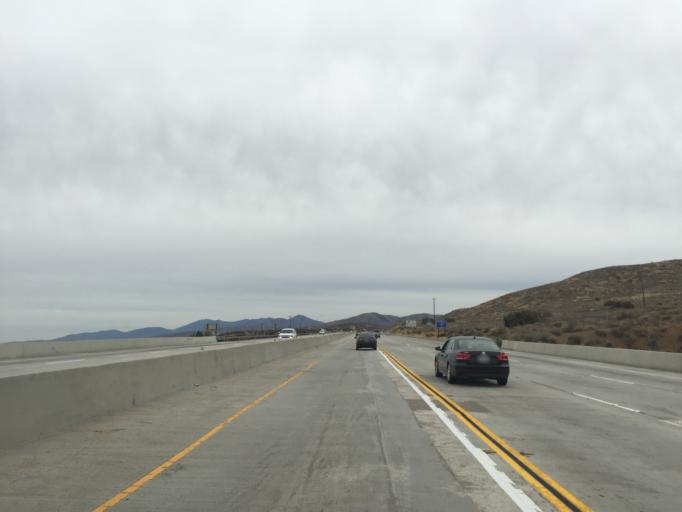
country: US
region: California
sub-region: Los Angeles County
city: Palmdale
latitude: 34.5447
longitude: -118.1278
